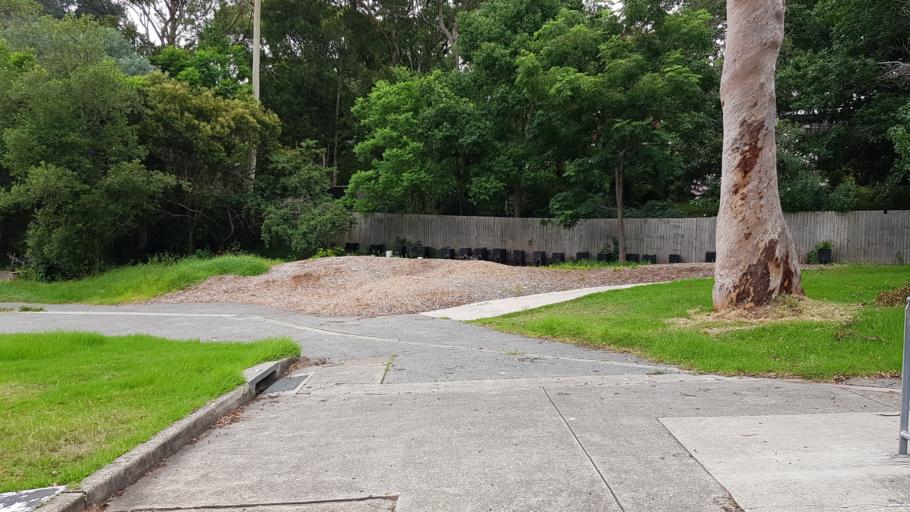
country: AU
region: New South Wales
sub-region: Pittwater
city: North Narrabeen
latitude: -33.7045
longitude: 151.2844
